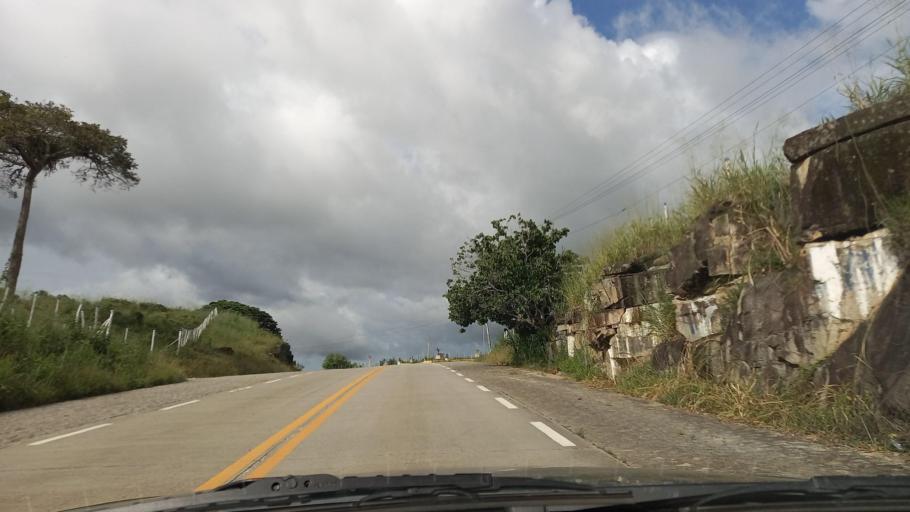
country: BR
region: Pernambuco
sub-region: Maraial
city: Maraial
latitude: -8.7902
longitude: -35.8821
